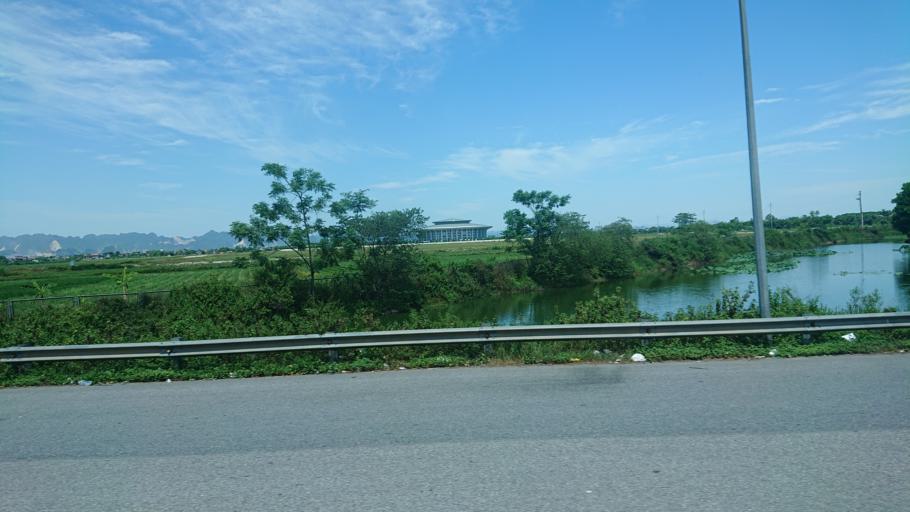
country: VN
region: Ha Nam
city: Thanh Pho Phu Ly
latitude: 20.5699
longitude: 105.9511
